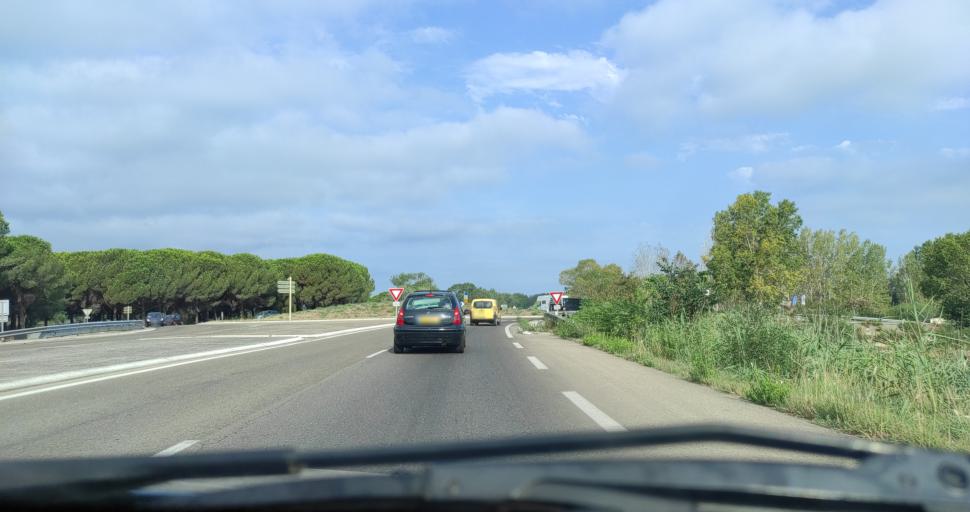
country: FR
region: Languedoc-Roussillon
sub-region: Departement du Gard
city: Le Grau-du-Roi
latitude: 43.5656
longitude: 4.1251
